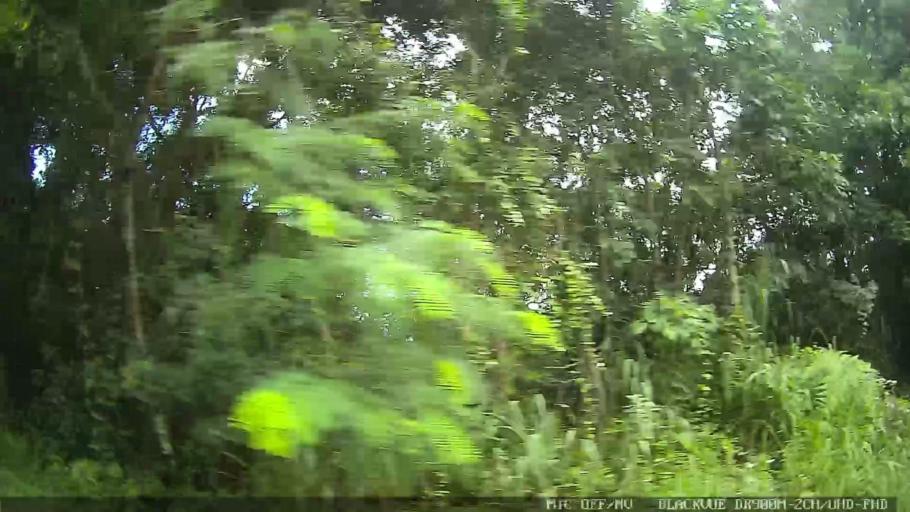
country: BR
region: Sao Paulo
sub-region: Iguape
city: Iguape
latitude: -24.6731
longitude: -47.4486
